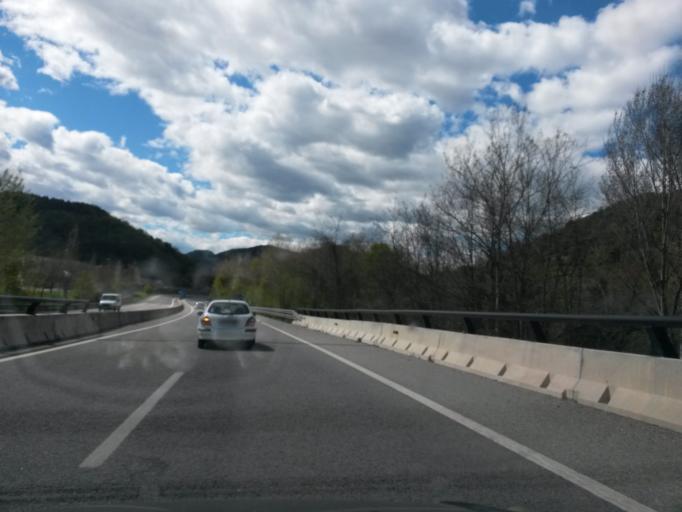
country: ES
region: Catalonia
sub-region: Provincia de Girona
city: Sant Joan les Fonts
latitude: 42.1944
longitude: 2.5086
